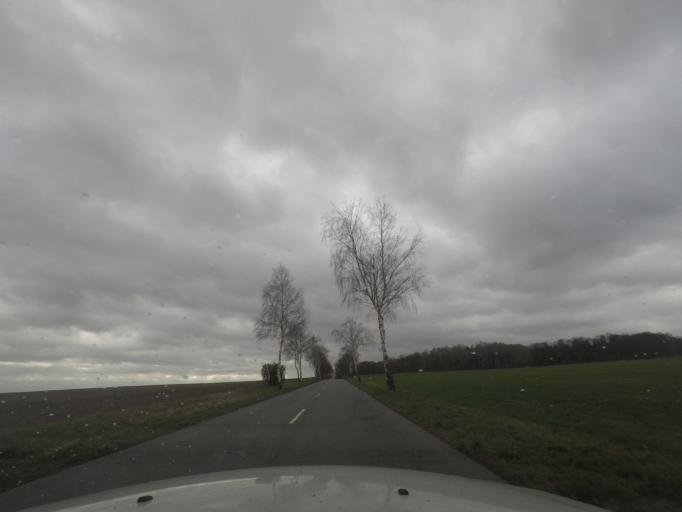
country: DE
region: Lower Saxony
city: Emmendorf
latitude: 53.0202
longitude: 10.6011
